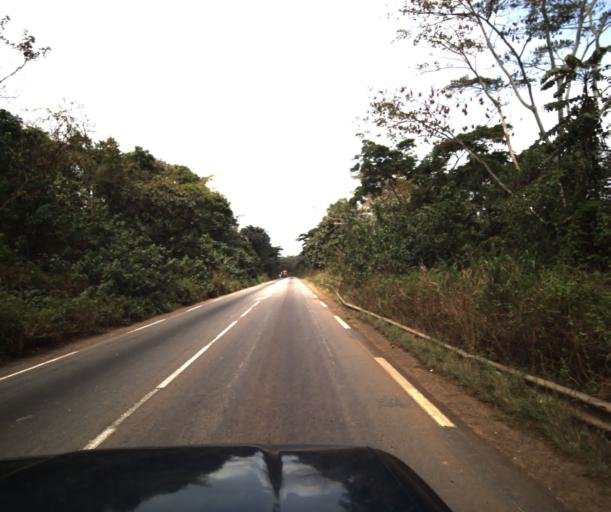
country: CM
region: Centre
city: Mbankomo
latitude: 3.7921
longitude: 11.2923
